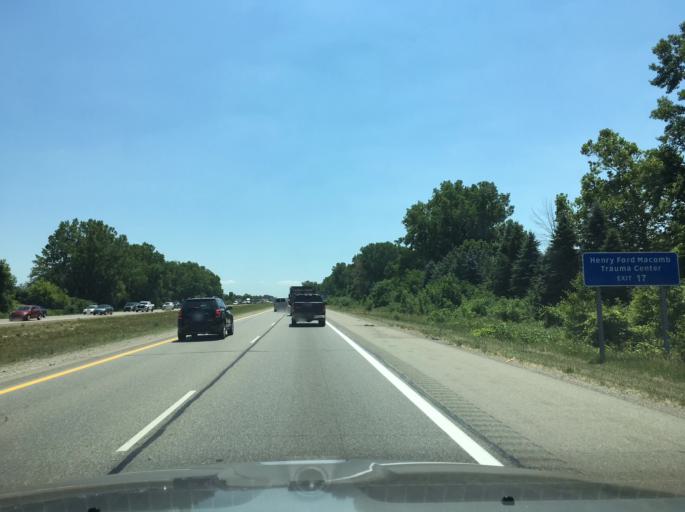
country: US
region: Michigan
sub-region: Macomb County
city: Utica
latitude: 42.6377
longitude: -83.0138
